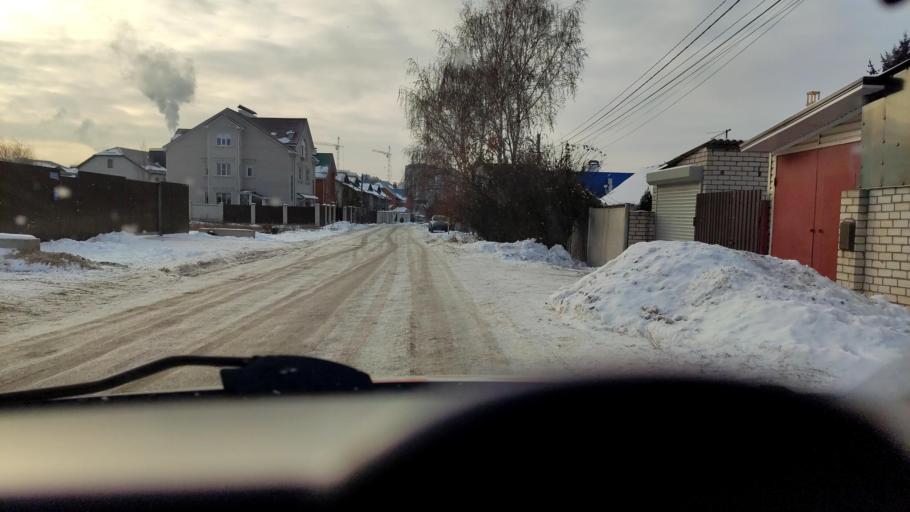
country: RU
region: Voronezj
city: Podgornoye
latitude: 51.7257
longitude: 39.1483
